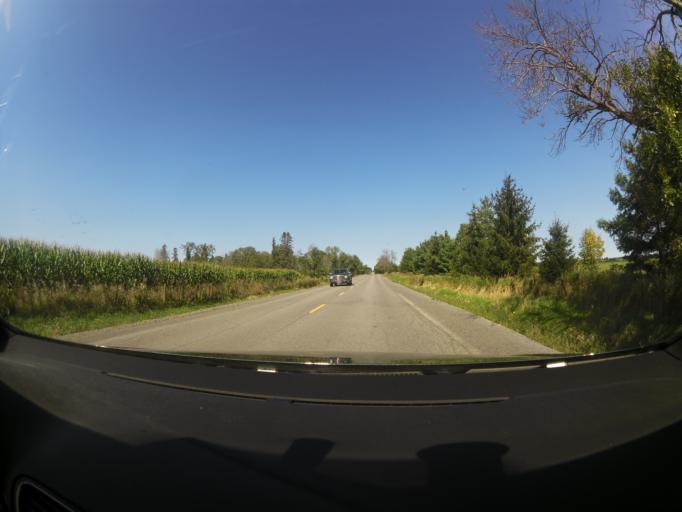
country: CA
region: Ontario
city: Arnprior
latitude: 45.3718
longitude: -76.2586
